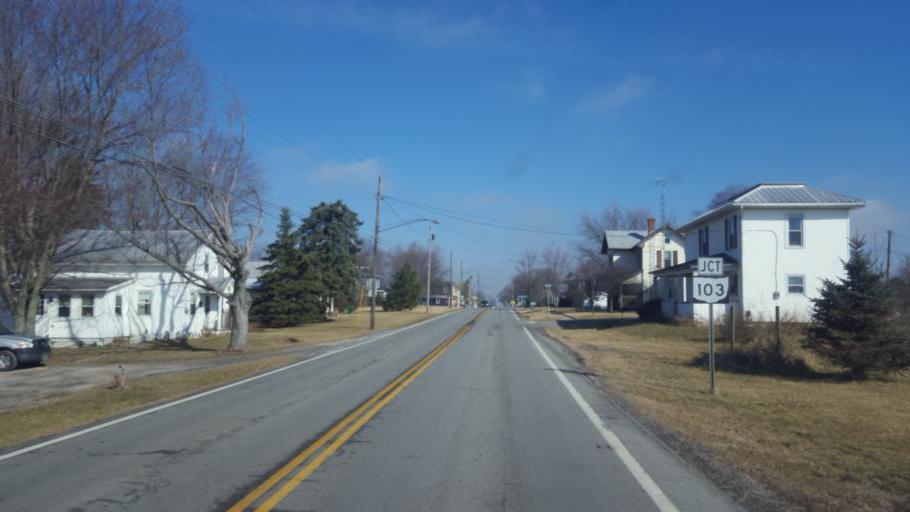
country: US
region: Ohio
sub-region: Crawford County
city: Bucyrus
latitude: 40.9481
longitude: -82.9450
